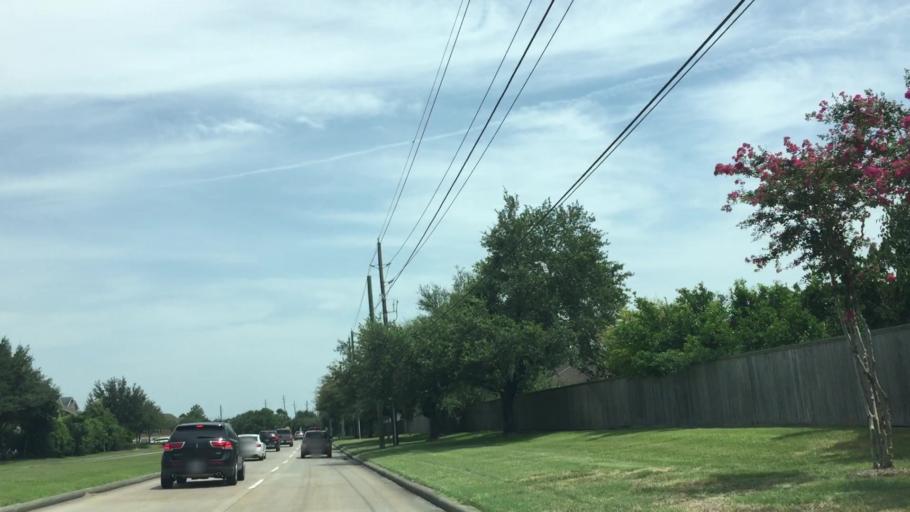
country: US
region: Texas
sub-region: Harris County
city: Jersey Village
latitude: 29.9061
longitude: -95.5610
